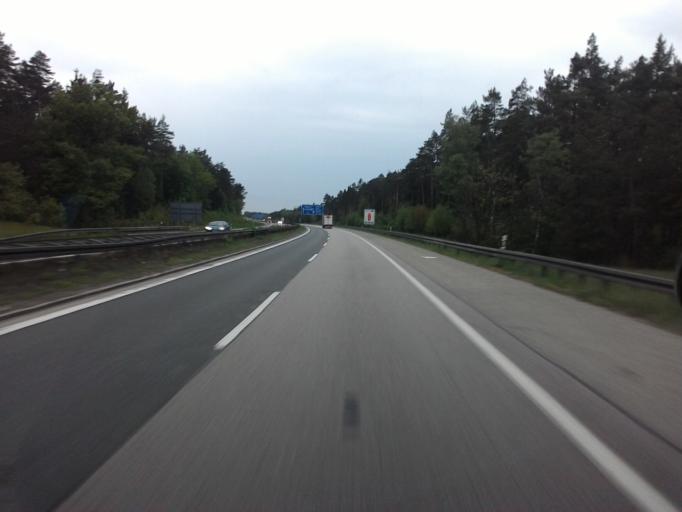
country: DE
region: Bavaria
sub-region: Regierungsbezirk Mittelfranken
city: Rothenbach an der Pegnitz
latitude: 49.4513
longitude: 11.2615
